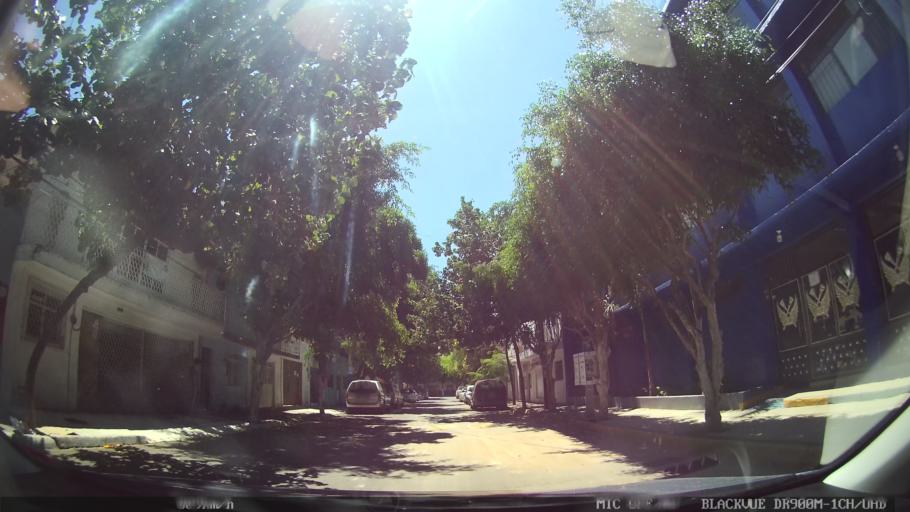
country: MX
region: Jalisco
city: Tlaquepaque
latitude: 20.6702
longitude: -103.2849
